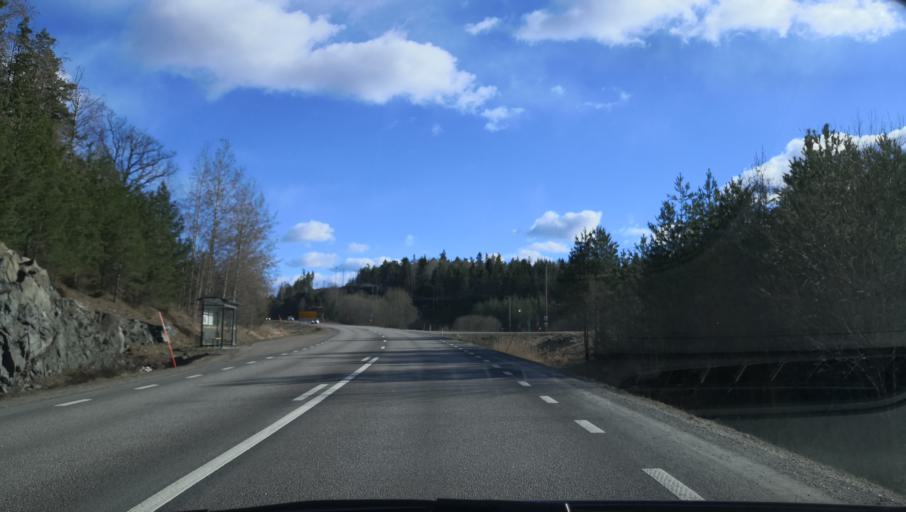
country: SE
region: Stockholm
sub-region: Varmdo Kommun
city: Gustavsberg
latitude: 59.2956
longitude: 18.3906
